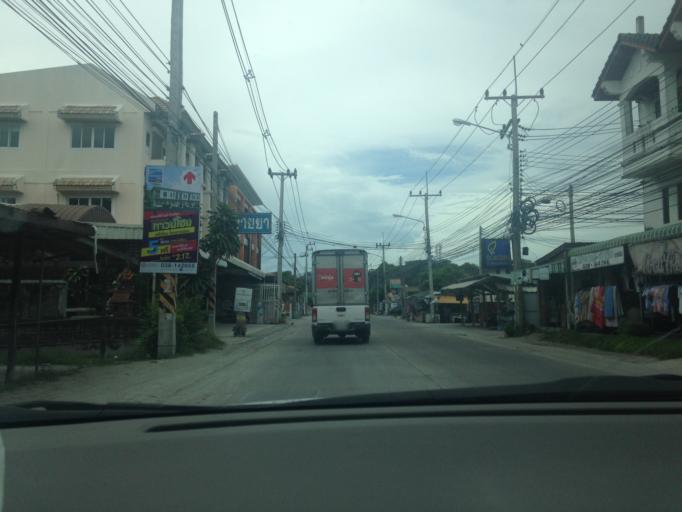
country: TH
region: Chon Buri
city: Chon Buri
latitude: 13.2991
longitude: 100.9347
